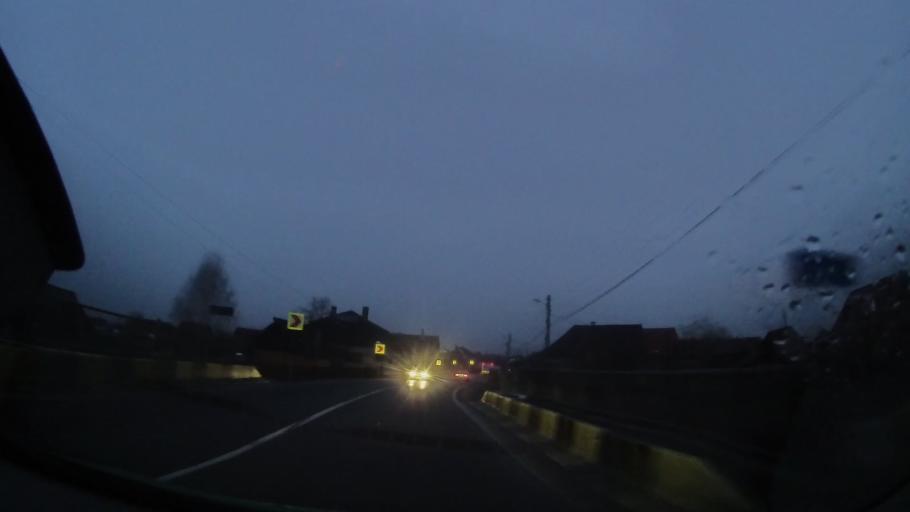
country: RO
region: Harghita
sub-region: Comuna Ditrau
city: Ditrau
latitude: 46.8073
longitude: 25.4930
